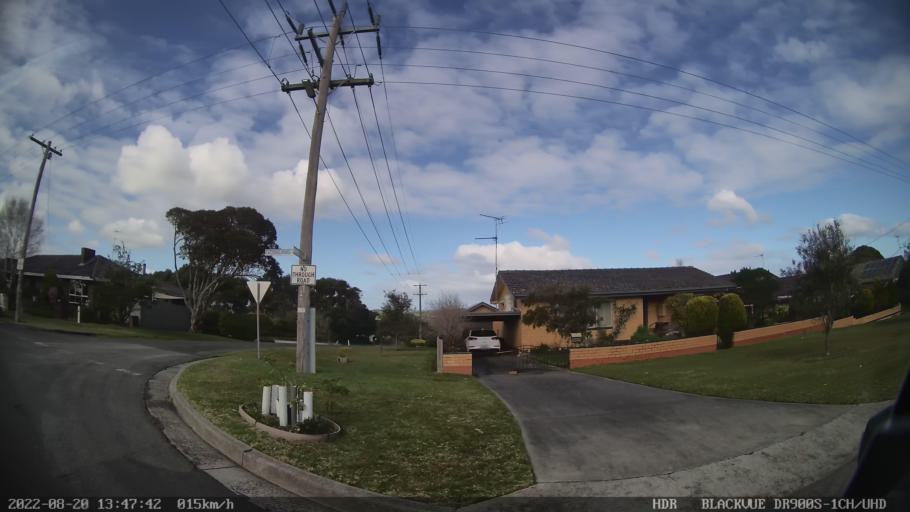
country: AU
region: Victoria
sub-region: Bass Coast
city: North Wonthaggi
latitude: -38.6029
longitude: 145.6035
